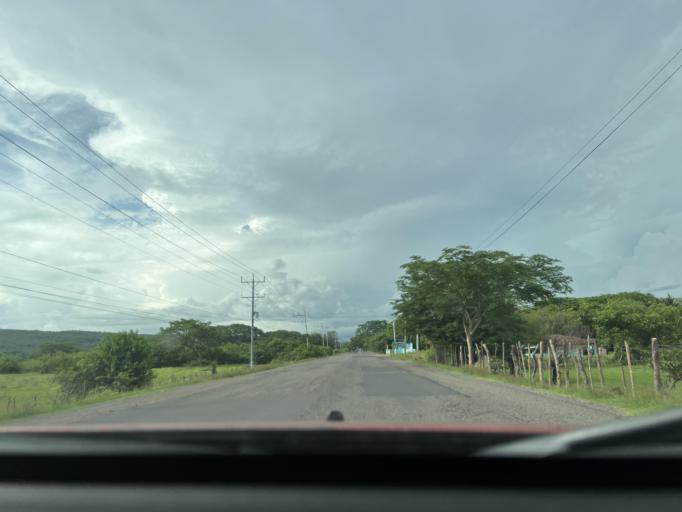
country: SV
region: La Union
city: San Alejo
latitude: 13.3803
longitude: -87.9070
